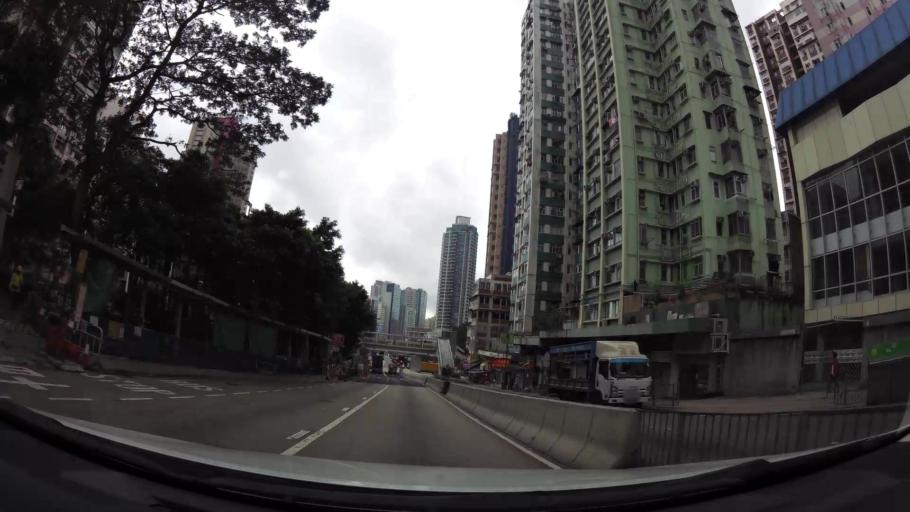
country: HK
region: Wong Tai Sin
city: Wong Tai Sin
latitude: 22.3443
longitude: 114.1990
